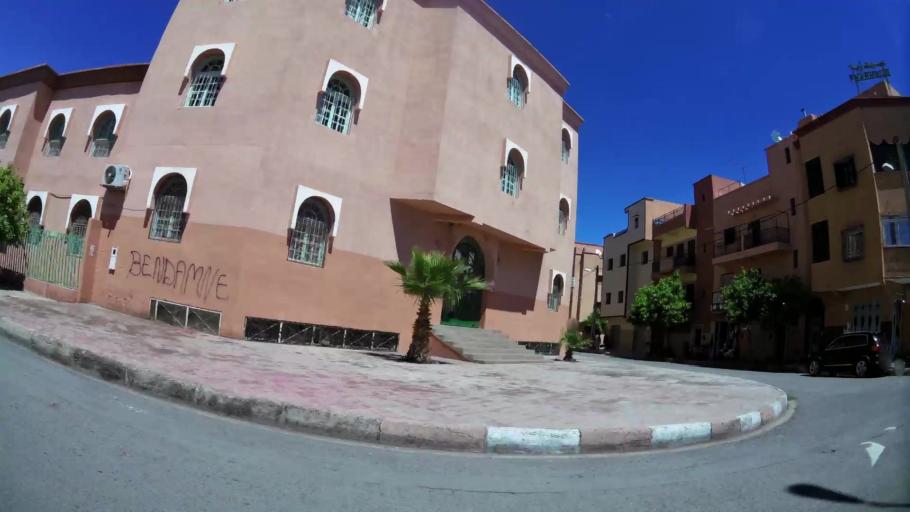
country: MA
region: Marrakech-Tensift-Al Haouz
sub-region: Marrakech
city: Marrakesh
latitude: 31.6303
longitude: -8.0553
